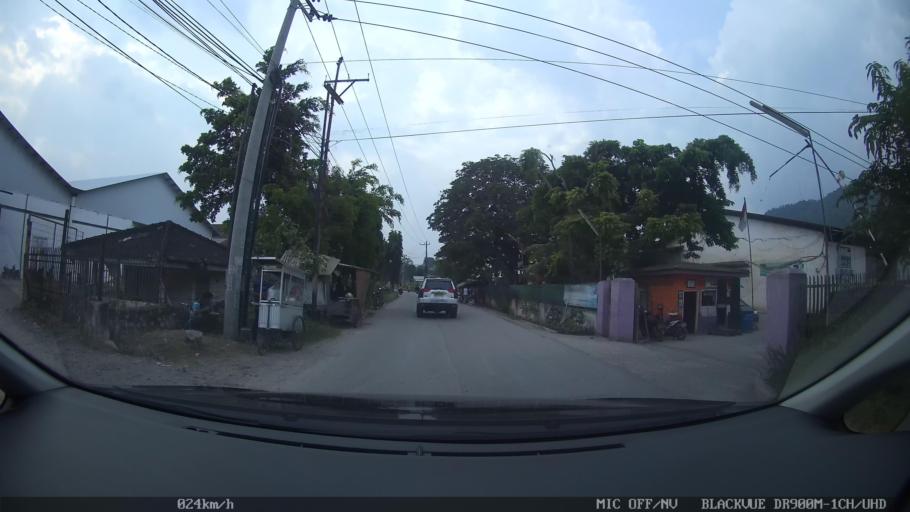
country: ID
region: Lampung
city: Panjang
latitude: -5.4450
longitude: 105.3022
